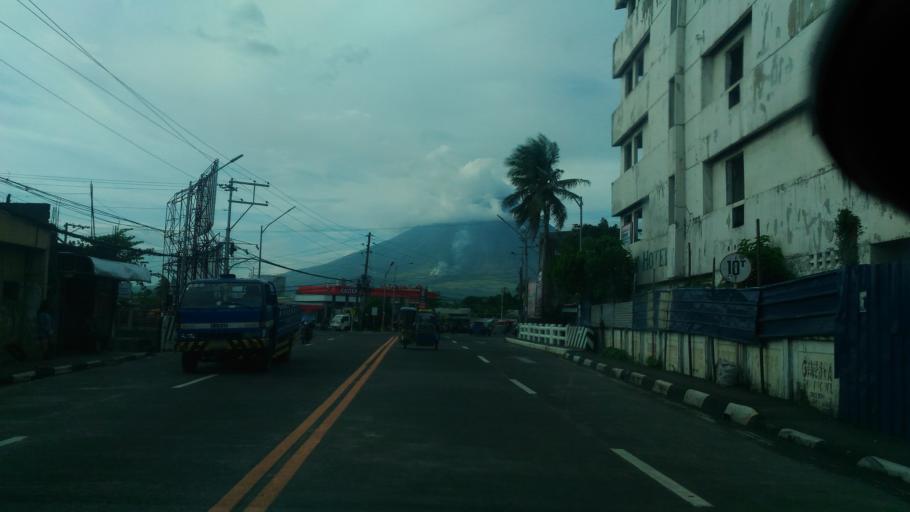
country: PH
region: Bicol
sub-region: Province of Albay
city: San Roque
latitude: 13.1540
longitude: 123.7518
